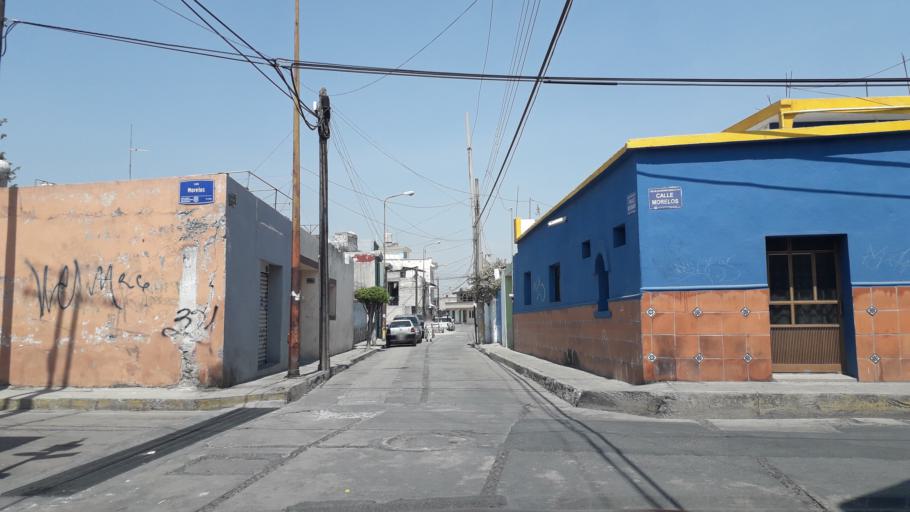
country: MX
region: Puebla
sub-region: Cuautlancingo
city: Sanctorum
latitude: 19.0905
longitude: -98.2175
